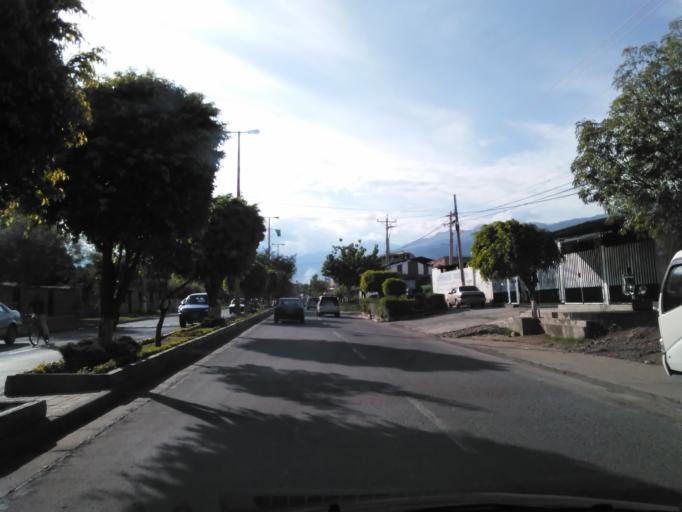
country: BO
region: Cochabamba
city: Cochabamba
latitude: -17.3502
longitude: -66.1936
